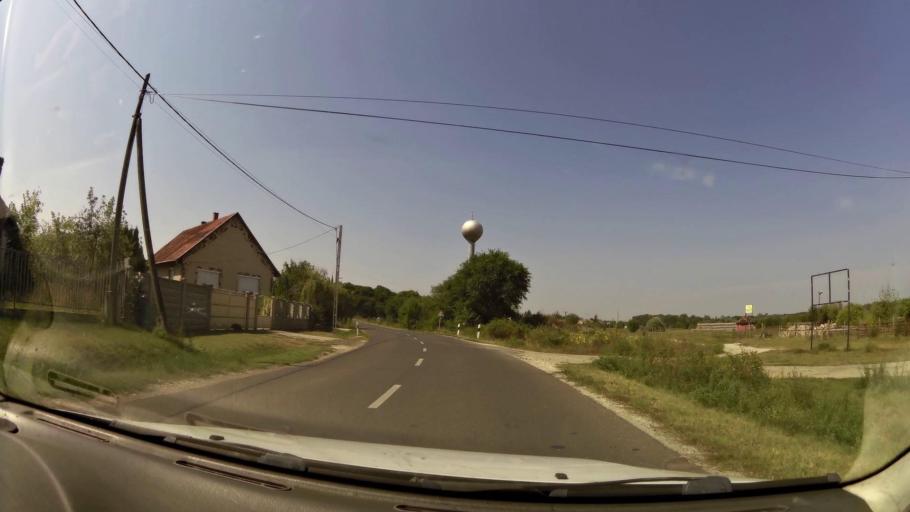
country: HU
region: Pest
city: Tapioszentmarton
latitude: 47.3477
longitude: 19.7523
